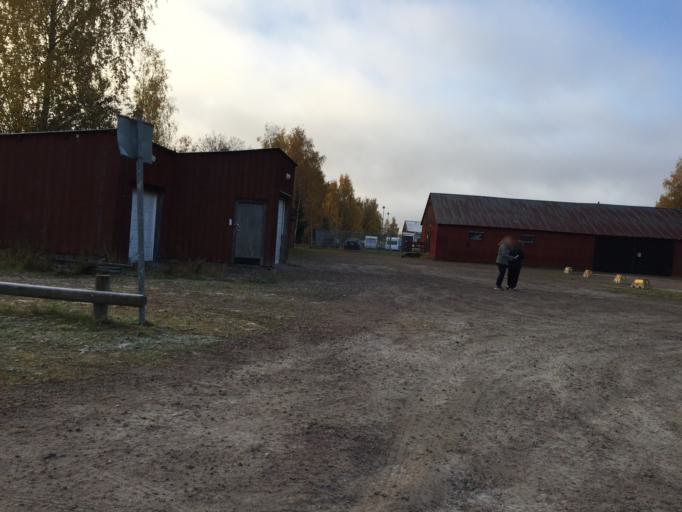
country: SE
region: Vaestmanland
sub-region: Hallstahammars Kommun
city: Hallstahammar
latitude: 59.6274
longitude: 16.2469
